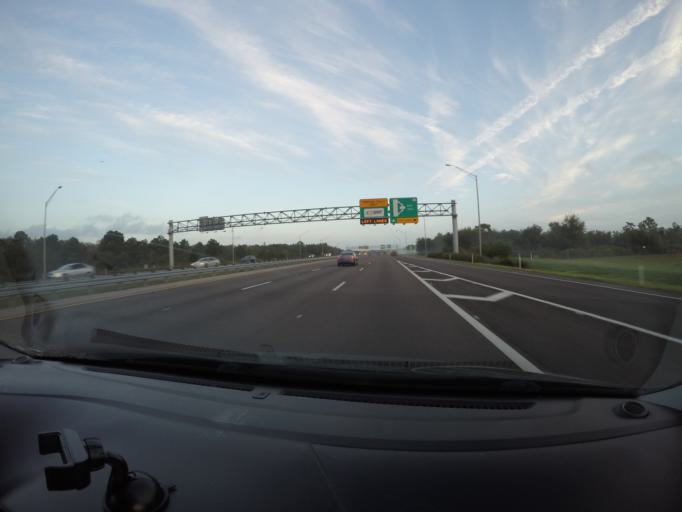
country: US
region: Florida
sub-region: Orange County
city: Azalea Park
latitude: 28.4819
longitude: -81.2405
